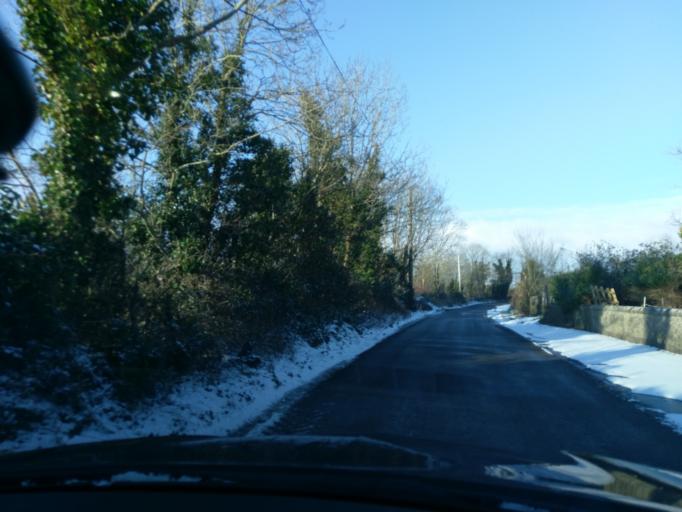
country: IE
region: Connaught
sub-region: County Galway
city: Athenry
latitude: 53.1833
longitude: -8.7272
